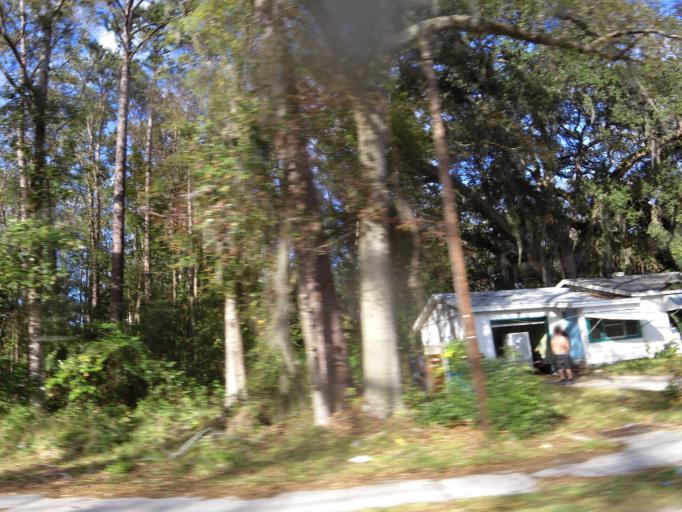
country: US
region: Florida
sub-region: Duval County
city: Jacksonville
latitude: 30.2871
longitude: -81.6179
